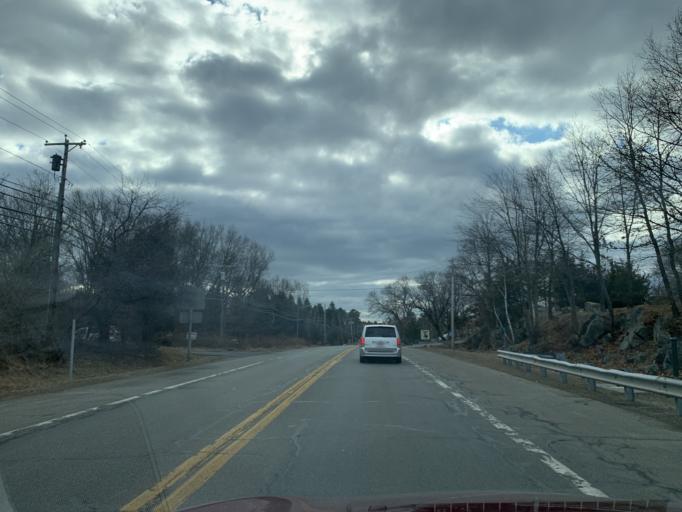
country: US
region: Massachusetts
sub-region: Essex County
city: Newburyport
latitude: 42.7887
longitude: -70.8790
